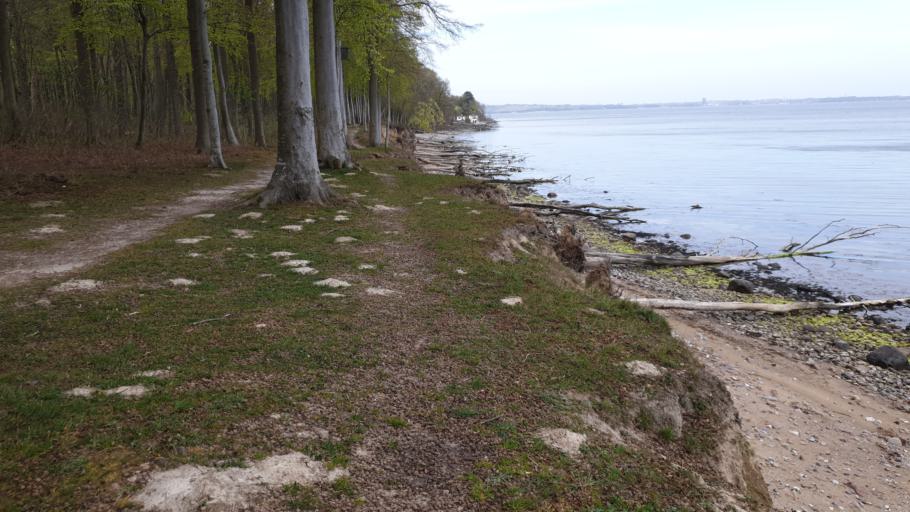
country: DK
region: South Denmark
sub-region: Sonderborg Kommune
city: Dybbol
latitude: 54.8532
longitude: 9.7593
